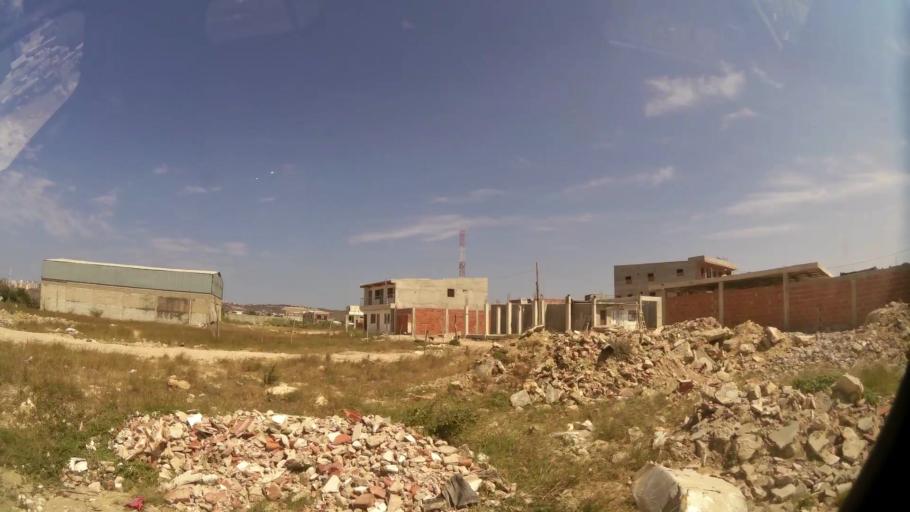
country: CO
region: Atlantico
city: Barranquilla
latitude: 10.9777
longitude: -74.8496
